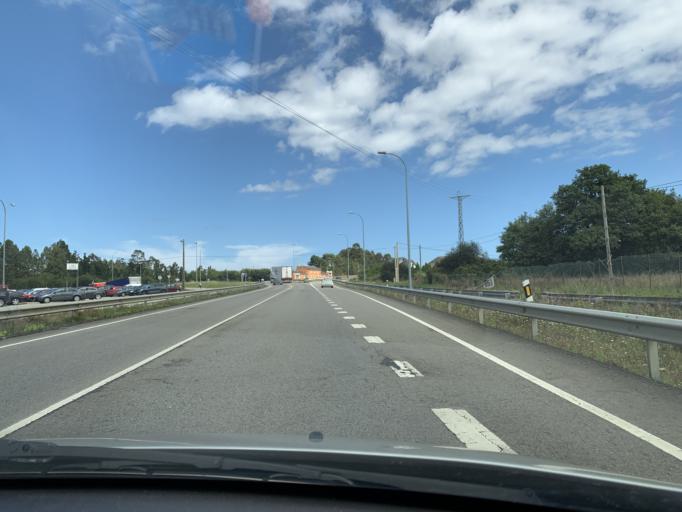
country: ES
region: Galicia
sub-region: Provincia de Lugo
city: Barreiros
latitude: 43.5389
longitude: -7.2535
